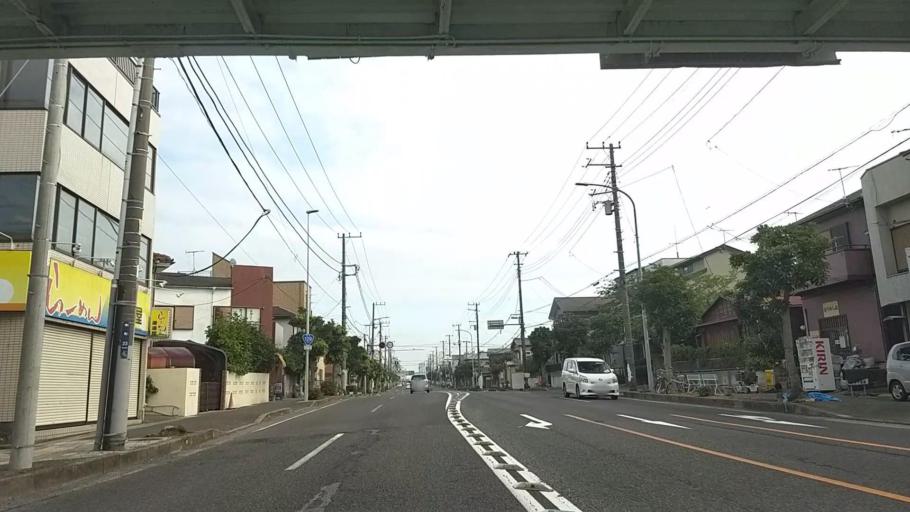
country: JP
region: Kanagawa
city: Hiratsuka
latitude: 35.3226
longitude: 139.3610
